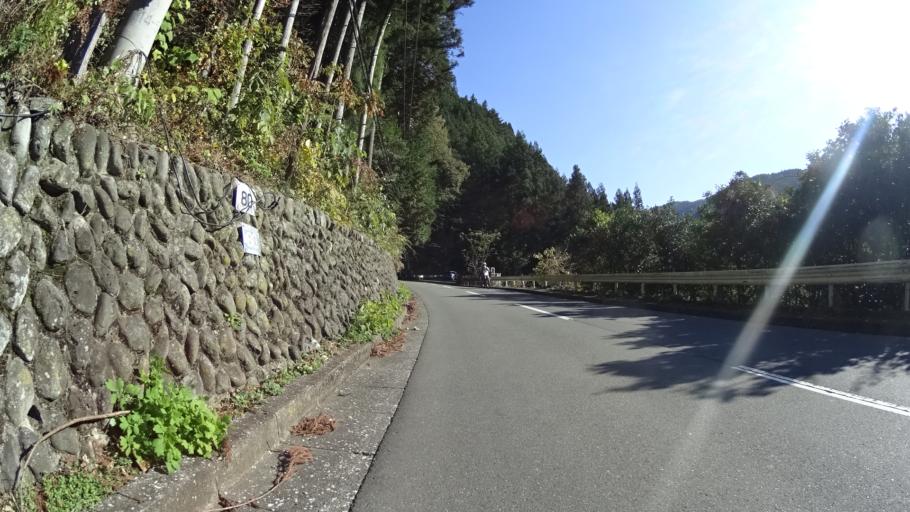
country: JP
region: Yamanashi
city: Uenohara
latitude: 35.7055
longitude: 139.1003
